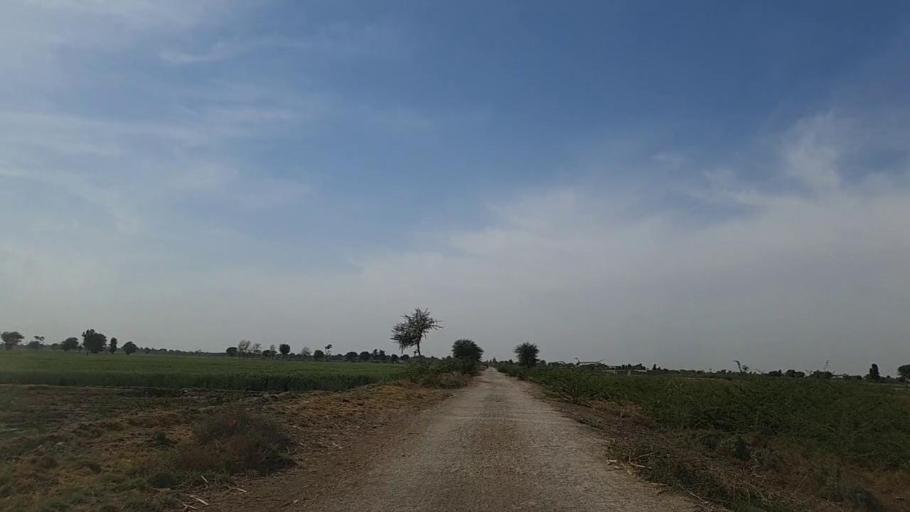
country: PK
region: Sindh
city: Samaro
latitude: 25.2278
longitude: 69.4377
